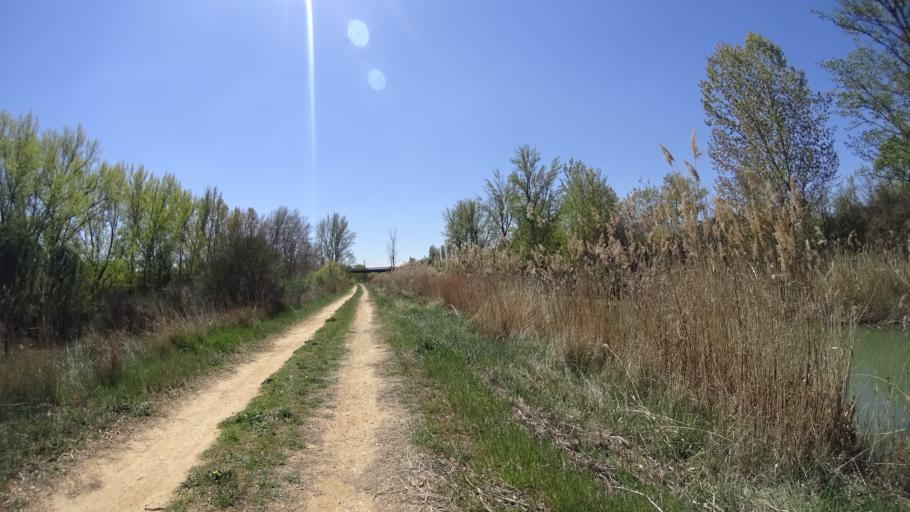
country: ES
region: Castille and Leon
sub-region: Provincia de Valladolid
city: Cubillas de Santa Marta
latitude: 41.8080
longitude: -4.5811
